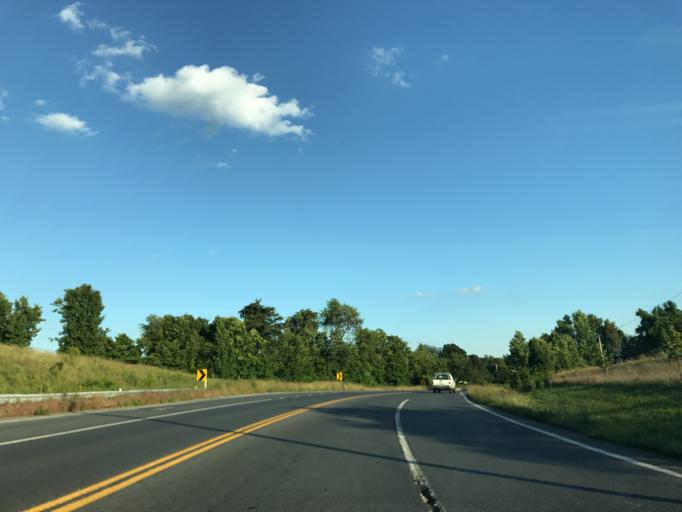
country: US
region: Maryland
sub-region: Anne Arundel County
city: Davidsonville
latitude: 38.9545
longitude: -76.6423
